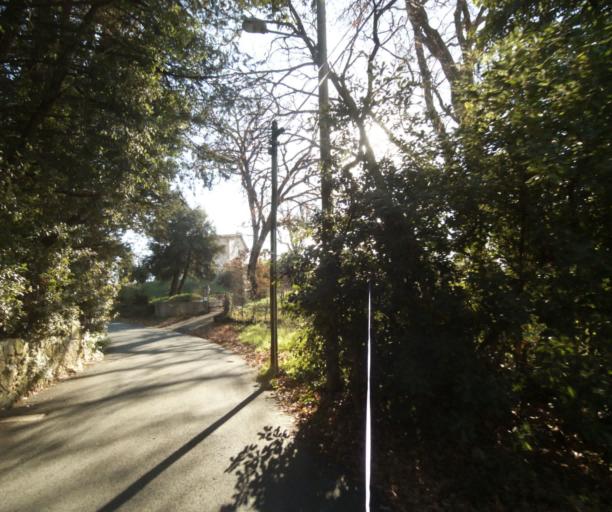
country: FR
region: Provence-Alpes-Cote d'Azur
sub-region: Departement des Alpes-Maritimes
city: Biot
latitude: 43.6140
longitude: 7.1035
